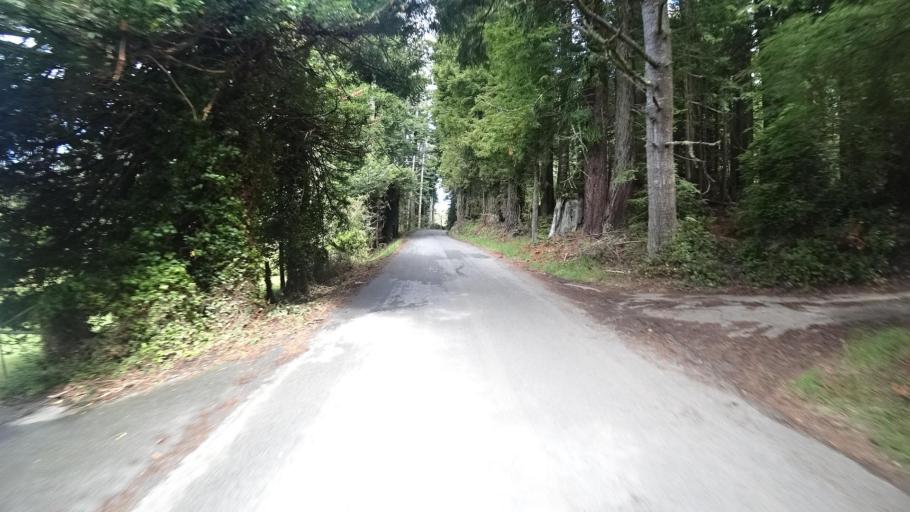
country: US
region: California
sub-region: Humboldt County
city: Bayside
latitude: 40.8590
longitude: -124.0390
